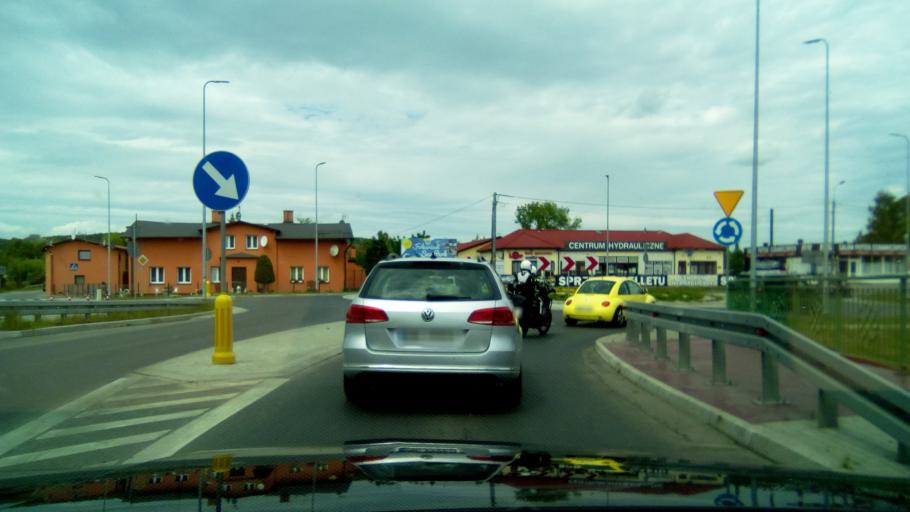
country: PL
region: Pomeranian Voivodeship
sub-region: Powiat leborski
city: Nowa Wies Leborska
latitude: 54.5578
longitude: 17.7277
